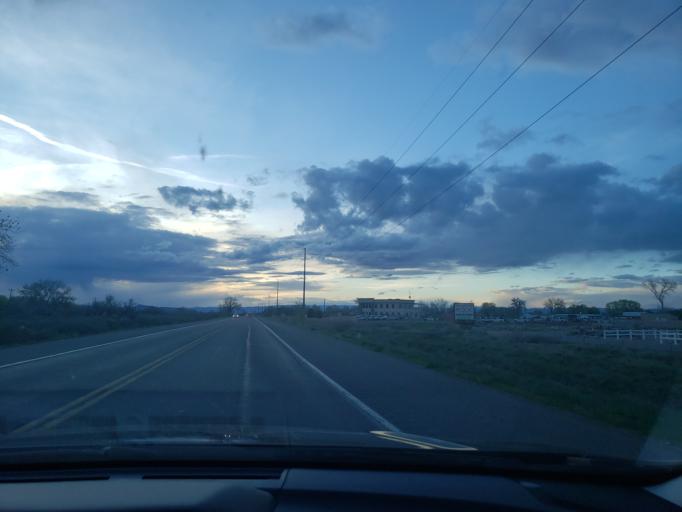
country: US
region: Colorado
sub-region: Mesa County
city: Fruita
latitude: 39.1330
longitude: -108.6894
